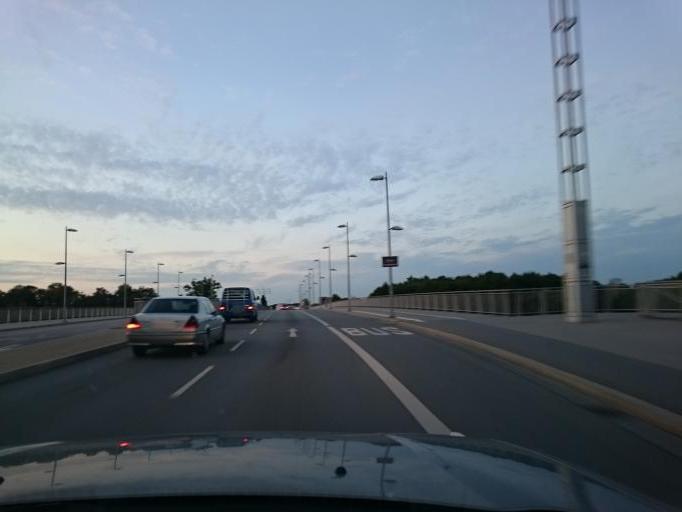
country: DE
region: Bavaria
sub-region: Upper Palatinate
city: Regensburg
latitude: 49.0184
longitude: 12.1126
